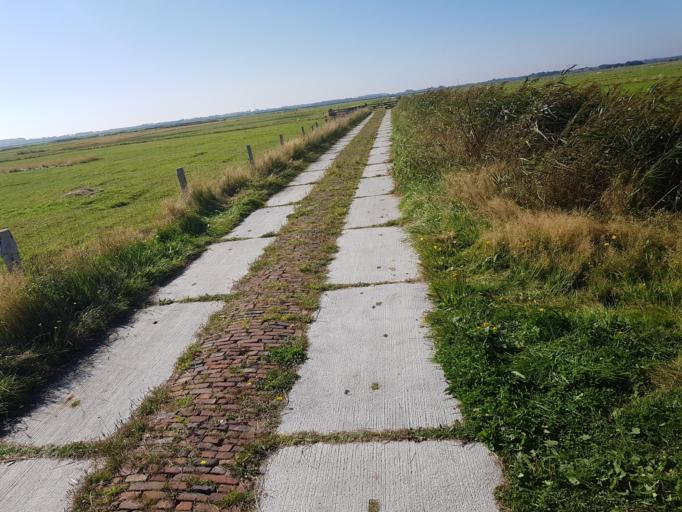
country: NL
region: North Holland
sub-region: Gemeente Texel
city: Den Burg
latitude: 53.0908
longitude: 4.8033
